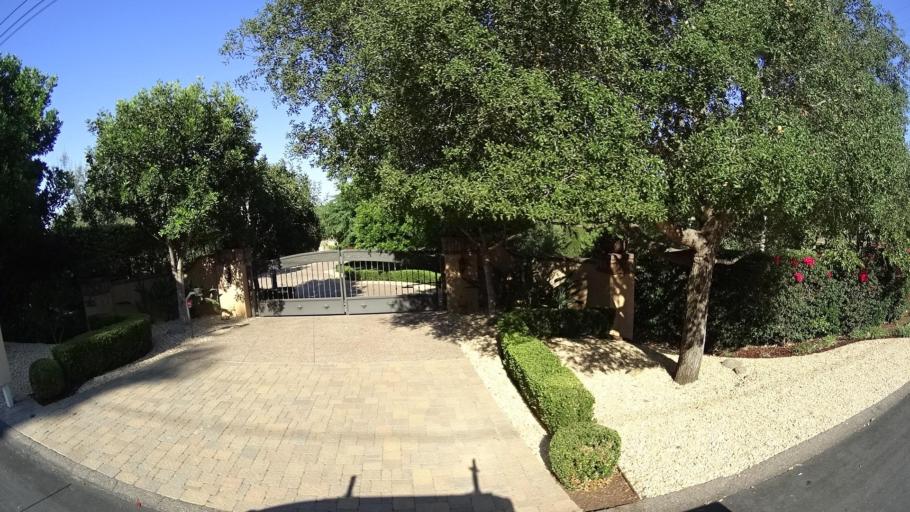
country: US
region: California
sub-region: San Diego County
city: Escondido
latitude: 33.0799
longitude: -117.0788
